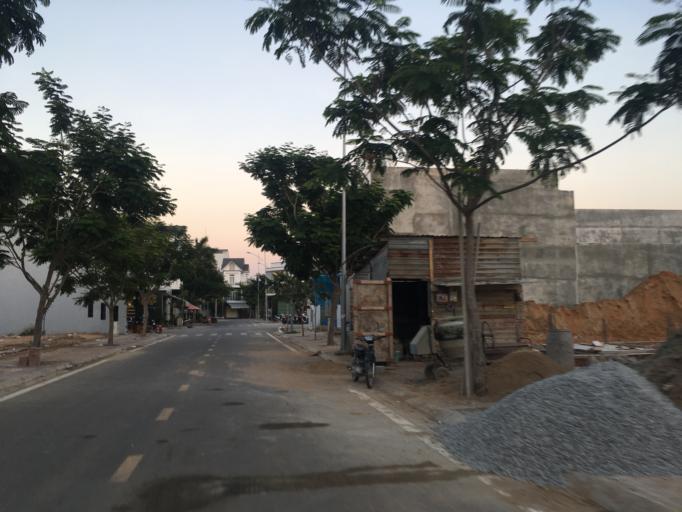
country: VN
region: Ninh Thuan
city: Phan Rang-Thap Cham
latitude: 11.5691
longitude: 108.9970
